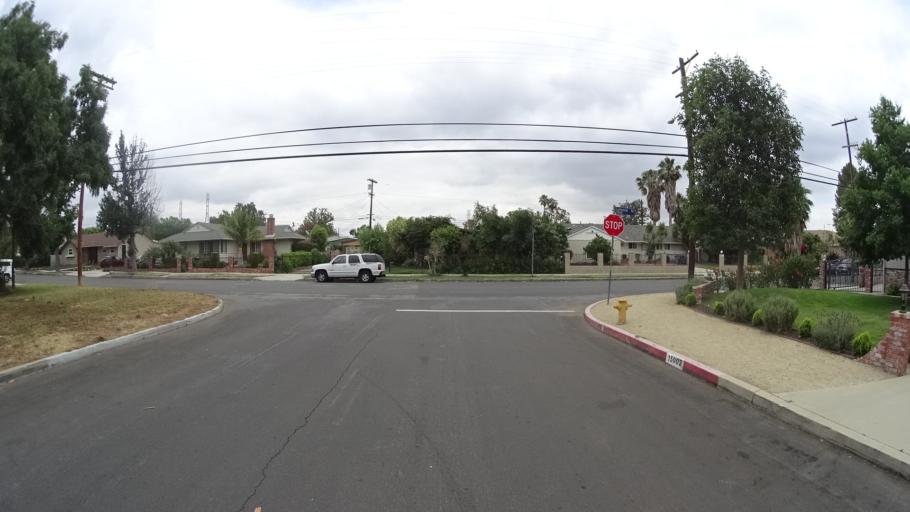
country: US
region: California
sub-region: Los Angeles County
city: San Fernando
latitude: 34.2633
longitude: -118.4590
